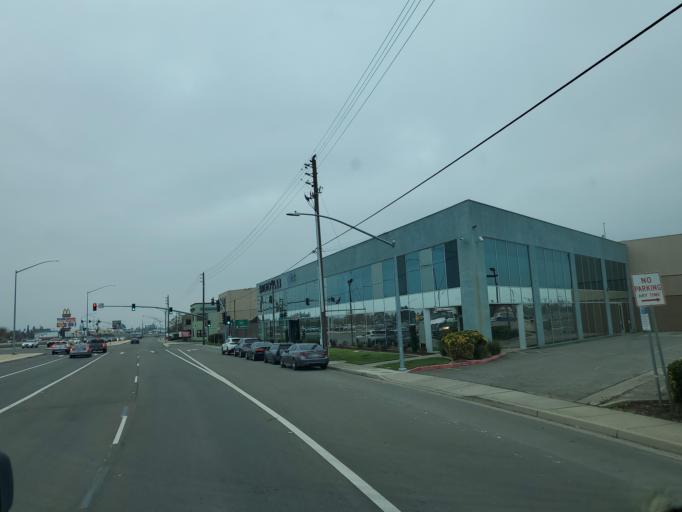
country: US
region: California
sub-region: Stanislaus County
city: Salida
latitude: 37.7011
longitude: -121.0697
